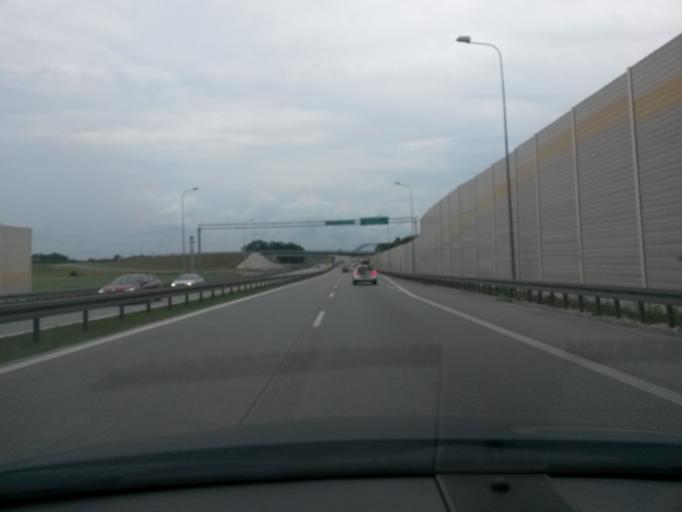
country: PL
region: Lodz Voivodeship
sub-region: Powiat skierniewicki
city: Kowiesy
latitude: 51.9211
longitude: 20.4577
